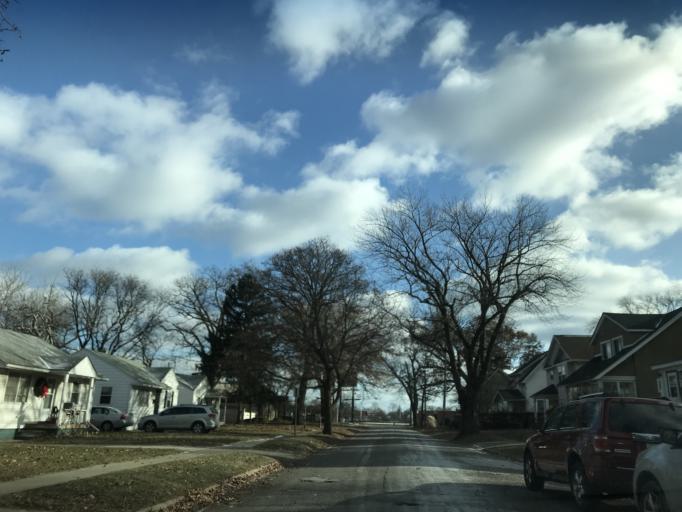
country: US
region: Michigan
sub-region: Oakland County
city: Hazel Park
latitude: 42.4590
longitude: -83.1070
